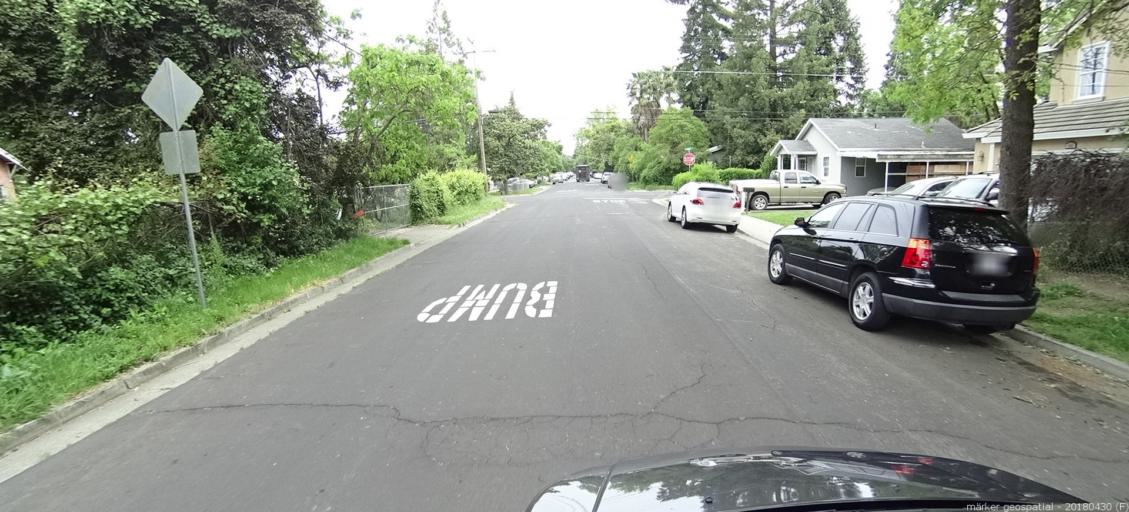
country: US
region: California
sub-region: Yolo County
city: West Sacramento
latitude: 38.5977
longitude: -121.5360
